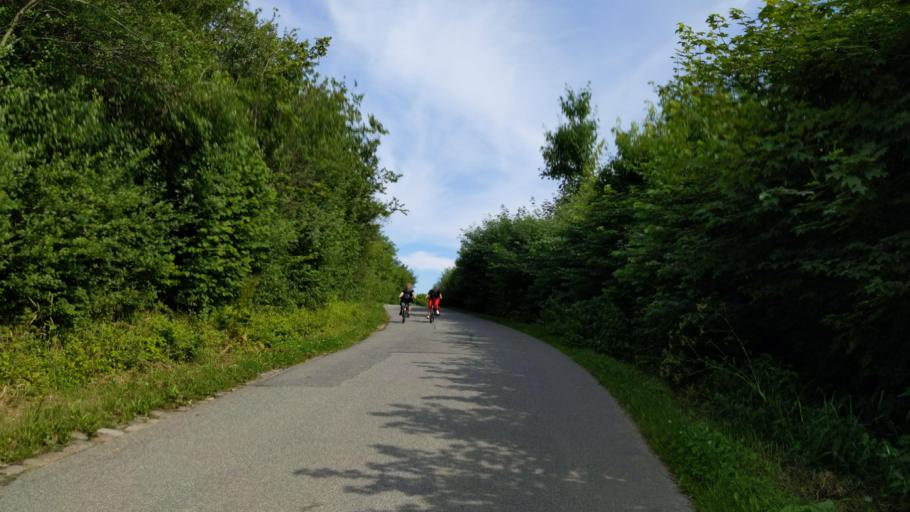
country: DE
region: Schleswig-Holstein
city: Eutin
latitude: 54.1070
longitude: 10.5986
